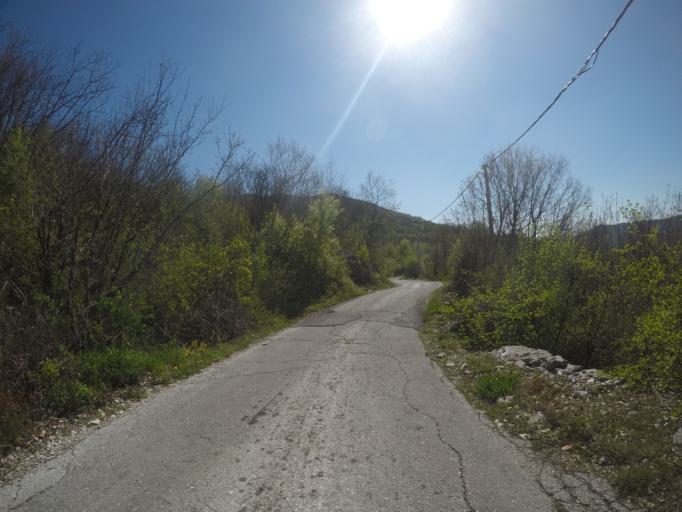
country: ME
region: Danilovgrad
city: Danilovgrad
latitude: 42.5263
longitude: 19.0458
